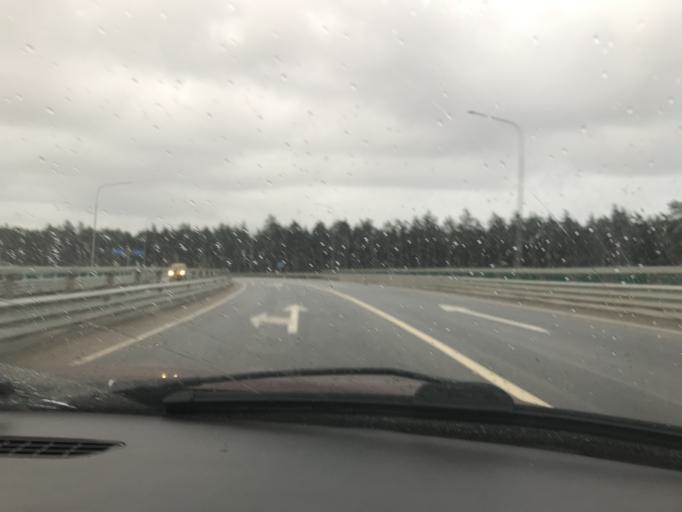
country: RU
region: Kaluga
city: Mstikhino
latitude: 54.5839
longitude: 36.0711
